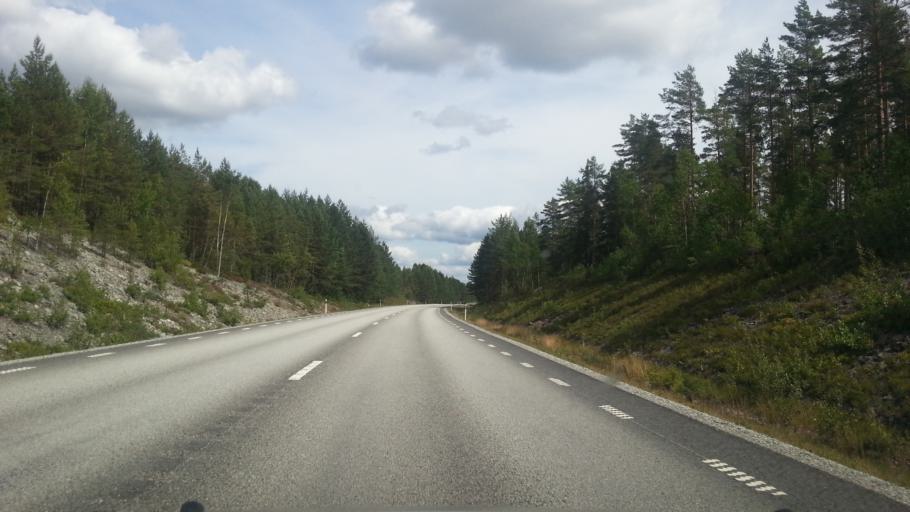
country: SE
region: Vaestmanland
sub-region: Skinnskattebergs Kommun
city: Skinnskatteberg
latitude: 59.7652
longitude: 15.4877
